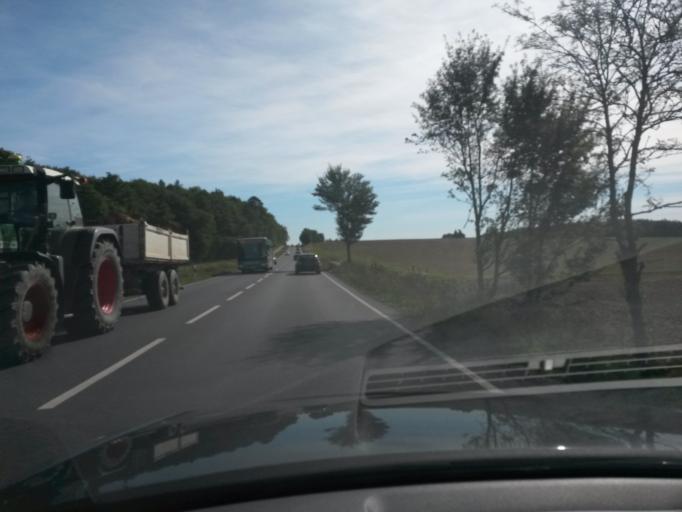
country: DE
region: Bavaria
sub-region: Regierungsbezirk Unterfranken
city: Kist
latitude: 49.7581
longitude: 9.8513
